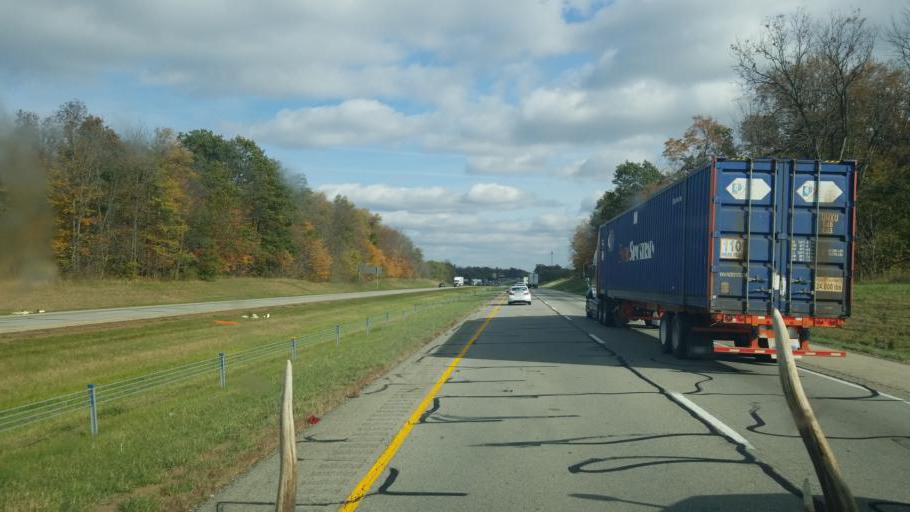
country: US
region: Indiana
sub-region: Wayne County
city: Cambridge City
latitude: 39.8528
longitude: -85.2378
